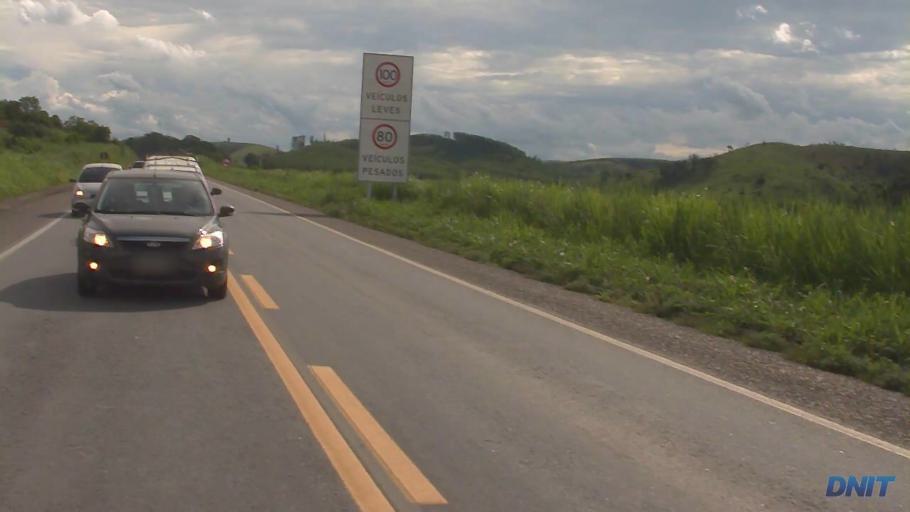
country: BR
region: Minas Gerais
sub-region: Belo Oriente
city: Belo Oriente
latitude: -19.2021
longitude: -42.2901
